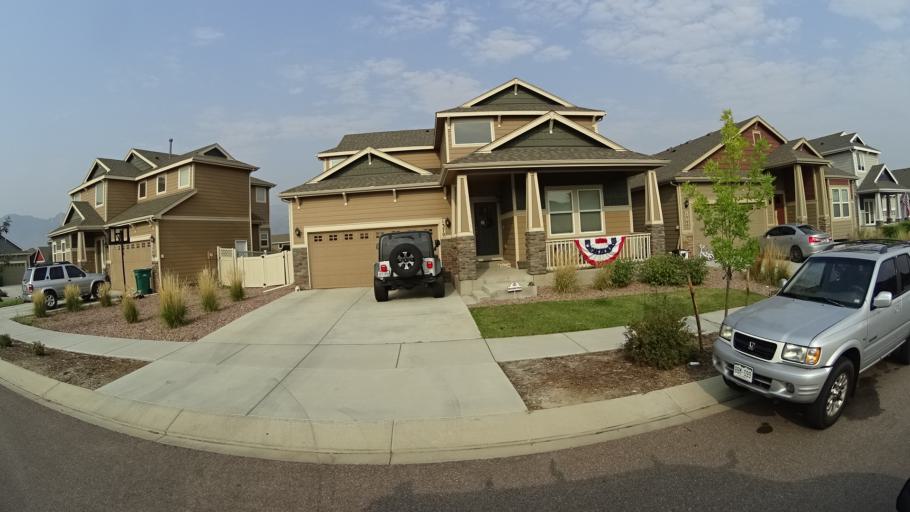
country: US
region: Colorado
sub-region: El Paso County
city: Stratmoor
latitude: 38.8132
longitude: -104.7847
